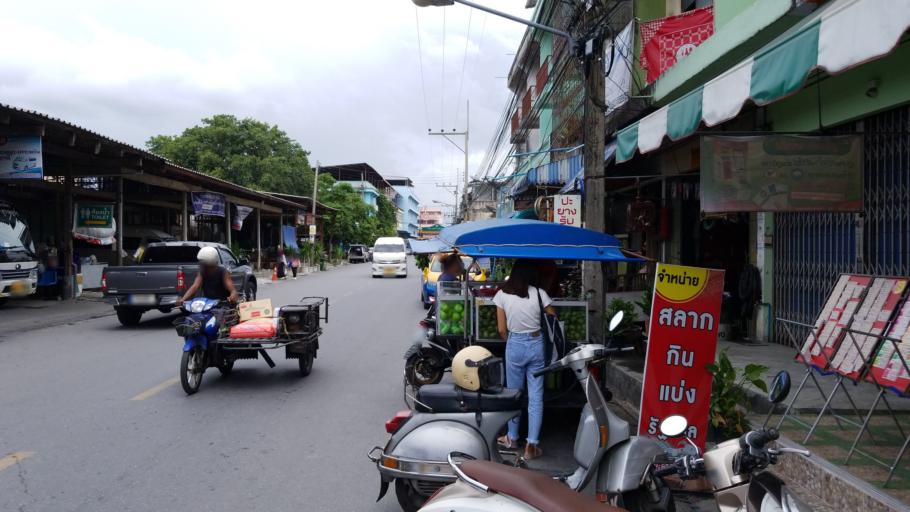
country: TH
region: Nakhon Si Thammarat
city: Nakhon Si Thammarat
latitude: 8.4349
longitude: 99.9523
